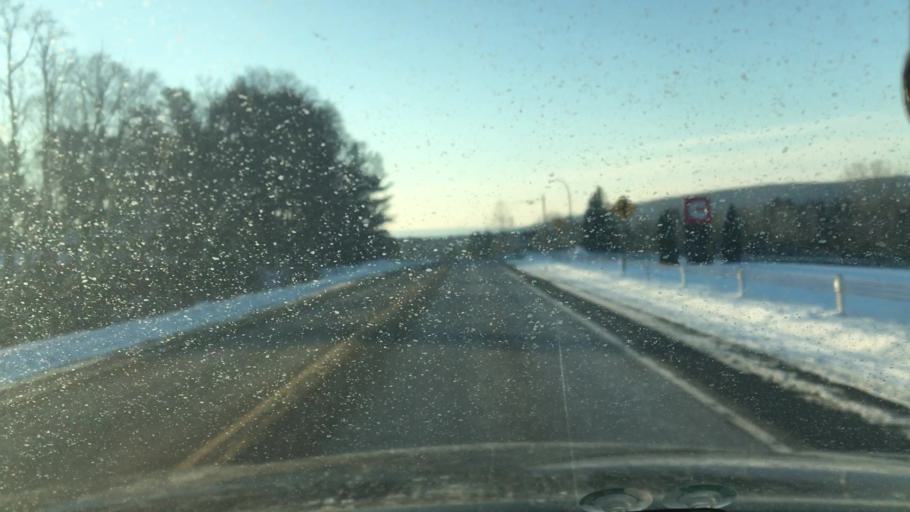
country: US
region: New York
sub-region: Chautauqua County
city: Lakewood
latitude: 42.0793
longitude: -79.3646
